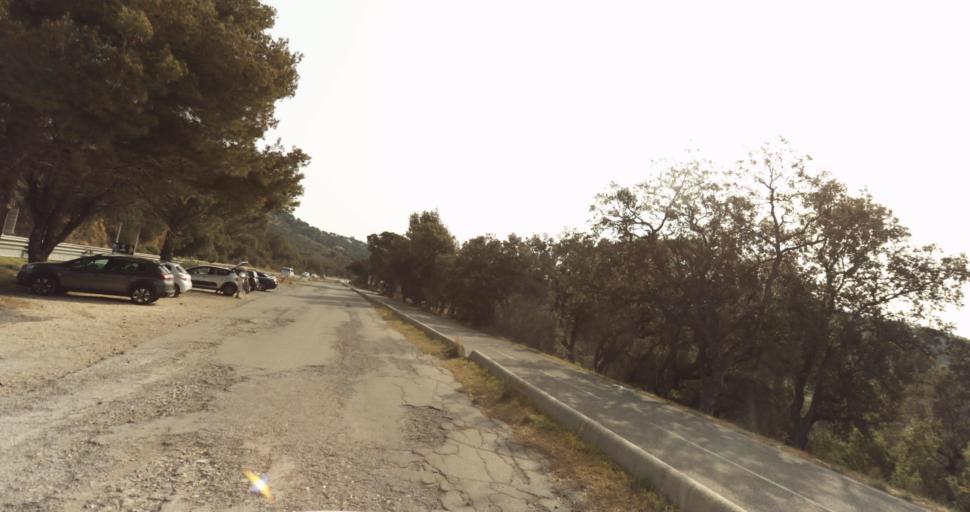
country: FR
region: Provence-Alpes-Cote d'Azur
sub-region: Departement du Var
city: Bormes-les-Mimosas
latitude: 43.1495
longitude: 6.2926
